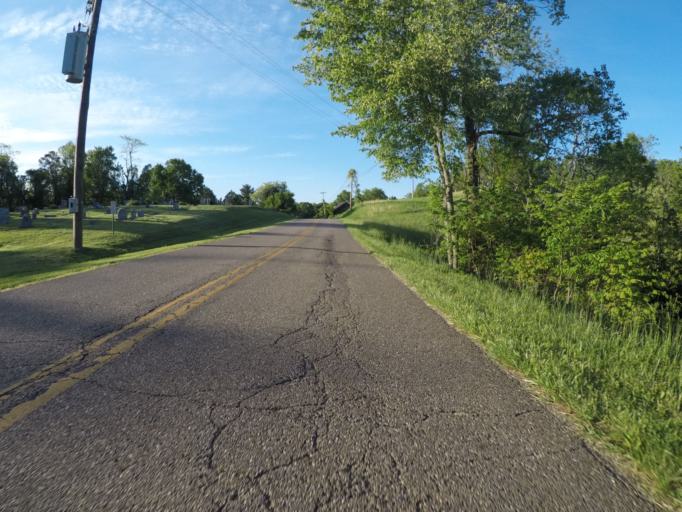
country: US
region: West Virginia
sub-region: Cabell County
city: Huntington
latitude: 38.5442
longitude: -82.4313
